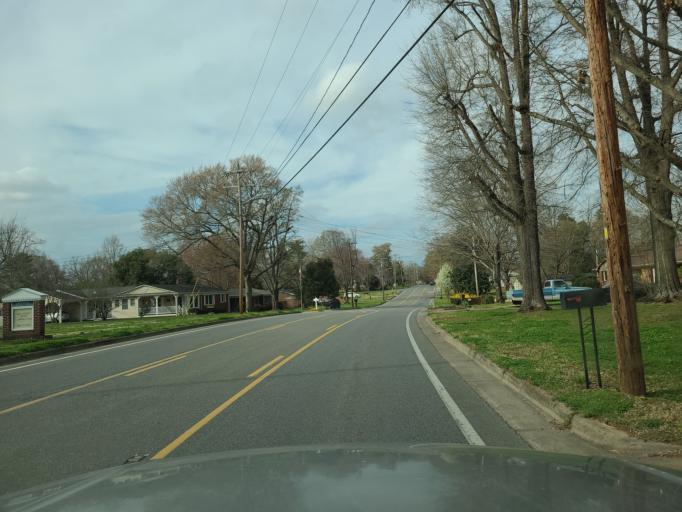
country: US
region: North Carolina
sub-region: Cleveland County
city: Shelby
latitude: 35.2821
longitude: -81.5625
